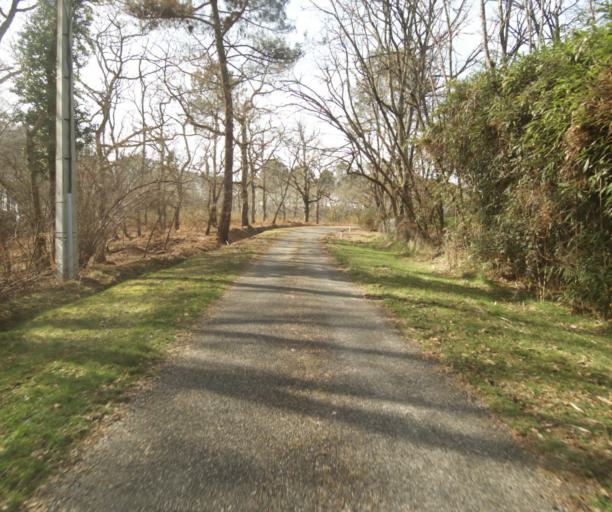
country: FR
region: Aquitaine
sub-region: Departement des Landes
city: Roquefort
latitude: 44.1359
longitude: -0.1983
